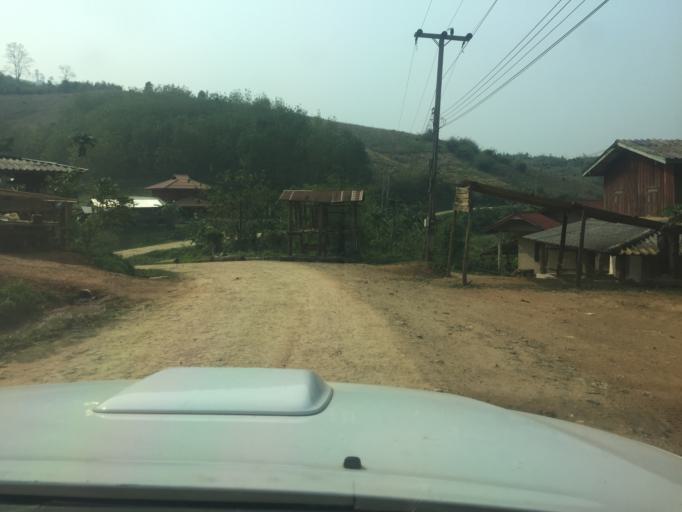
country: TH
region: Phayao
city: Phu Sang
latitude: 19.6575
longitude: 100.5287
